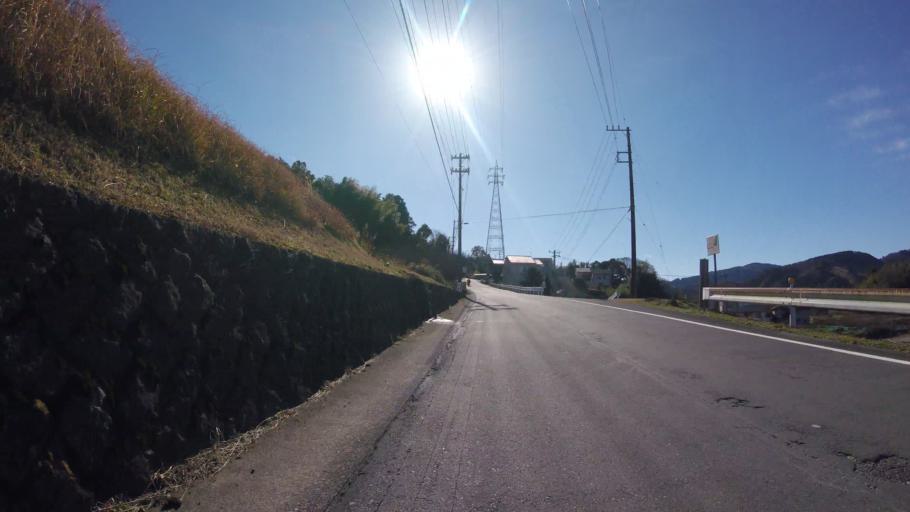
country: JP
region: Shizuoka
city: Ito
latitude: 34.9534
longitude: 138.9431
